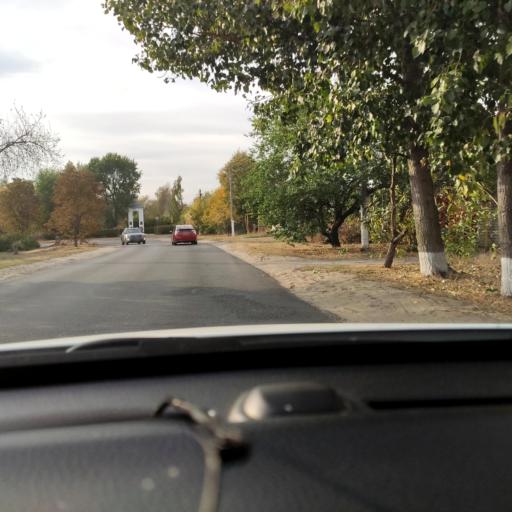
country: RU
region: Voronezj
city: Somovo
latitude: 51.6899
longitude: 39.3186
